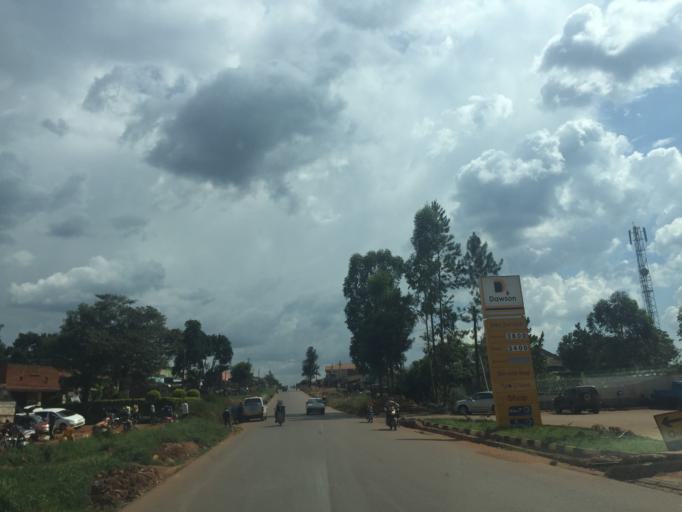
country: UG
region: Central Region
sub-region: Luwero District
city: Wobulenzi
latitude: 0.7230
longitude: 32.5282
